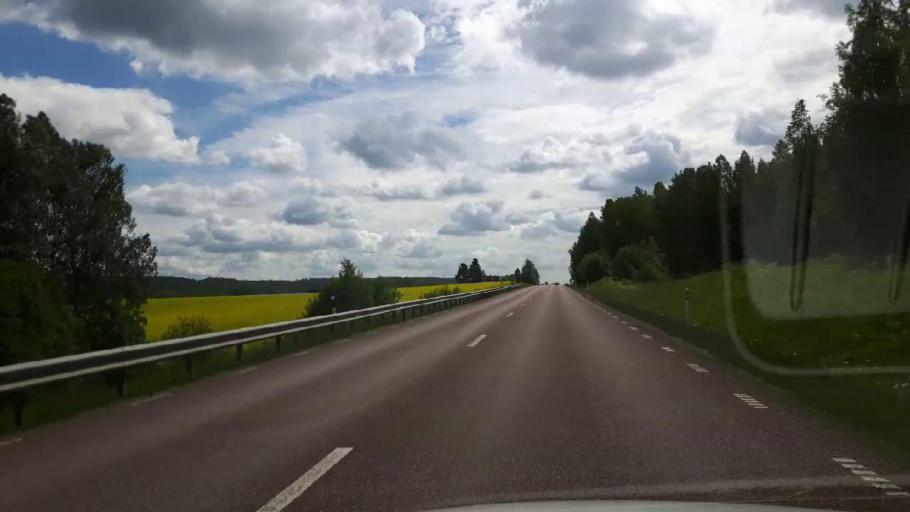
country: SE
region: Dalarna
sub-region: Hedemora Kommun
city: Langshyttan
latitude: 60.3803
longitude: 15.9104
